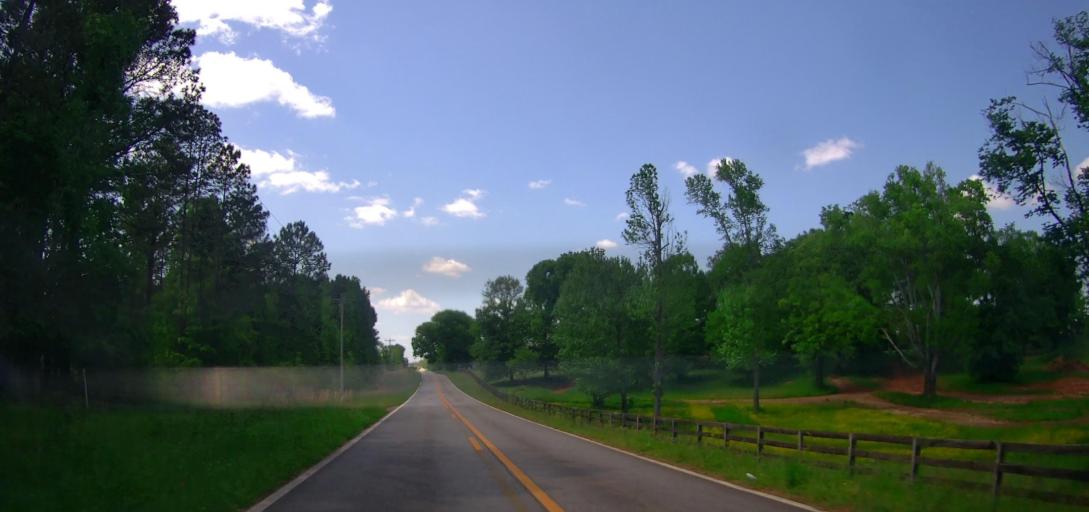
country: US
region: Georgia
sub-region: Putnam County
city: Eatonton
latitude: 33.3258
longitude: -83.3124
